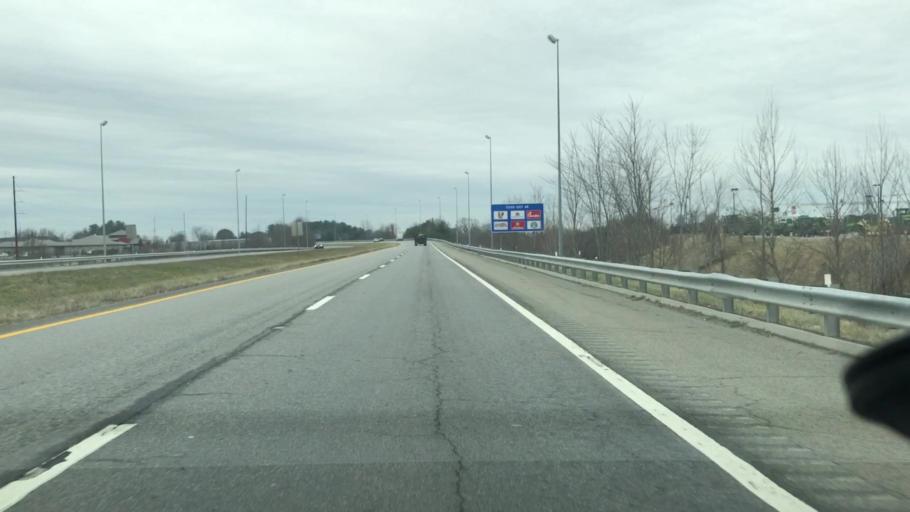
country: US
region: Virginia
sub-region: Montgomery County
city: Merrimac
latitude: 37.1773
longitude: -80.4127
